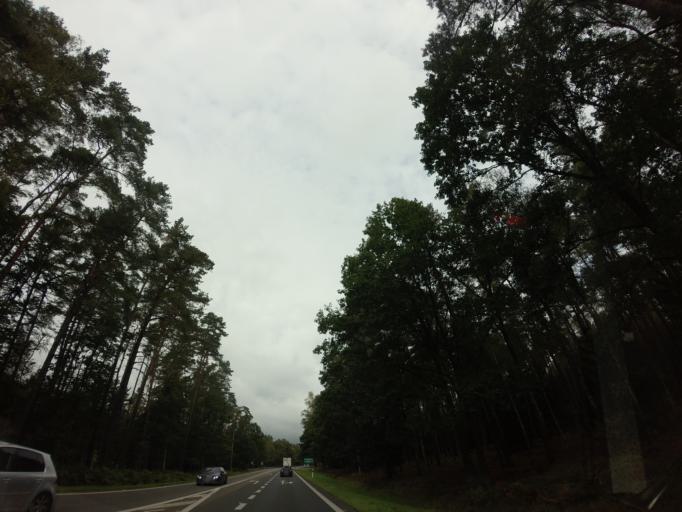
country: PL
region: West Pomeranian Voivodeship
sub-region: Powiat goleniowski
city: Przybiernow
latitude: 53.7123
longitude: 14.7752
